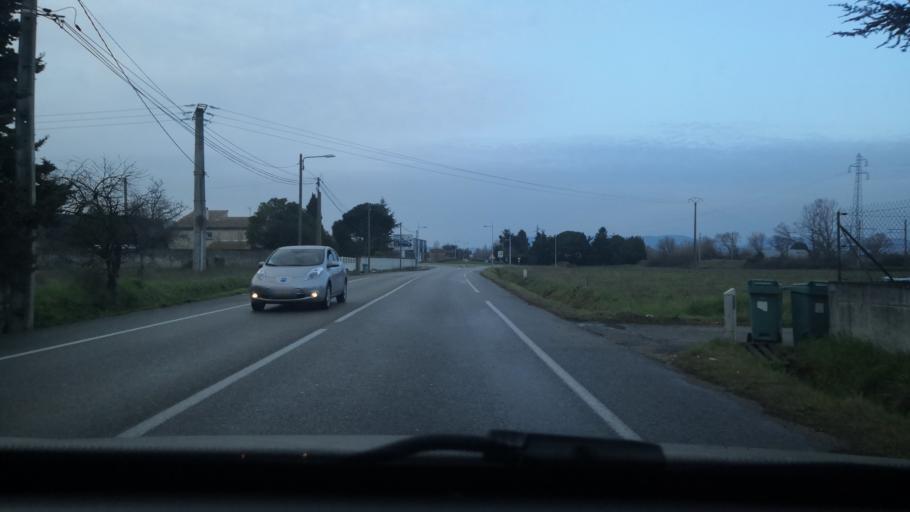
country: FR
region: Rhone-Alpes
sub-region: Departement de la Drome
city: Montelimar
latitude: 44.5295
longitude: 4.7357
